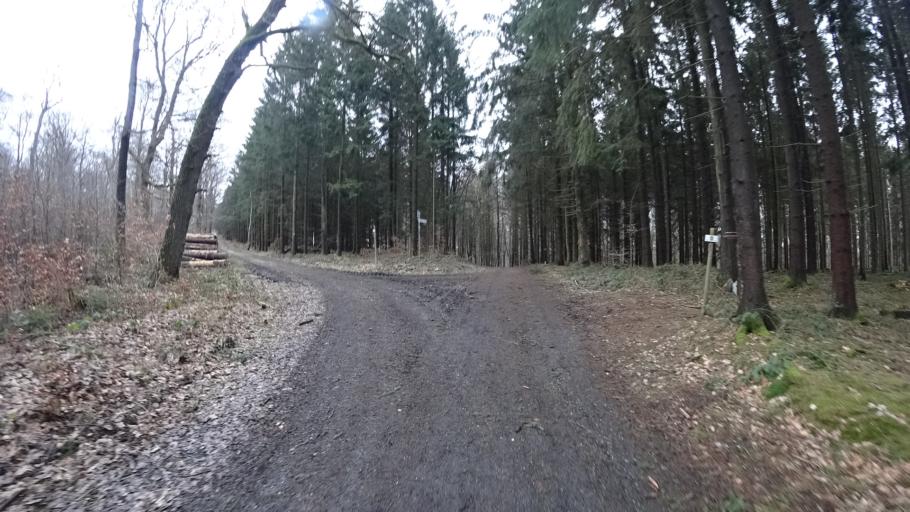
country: DE
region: Rheinland-Pfalz
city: Hillscheid
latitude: 50.4041
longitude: 7.7063
